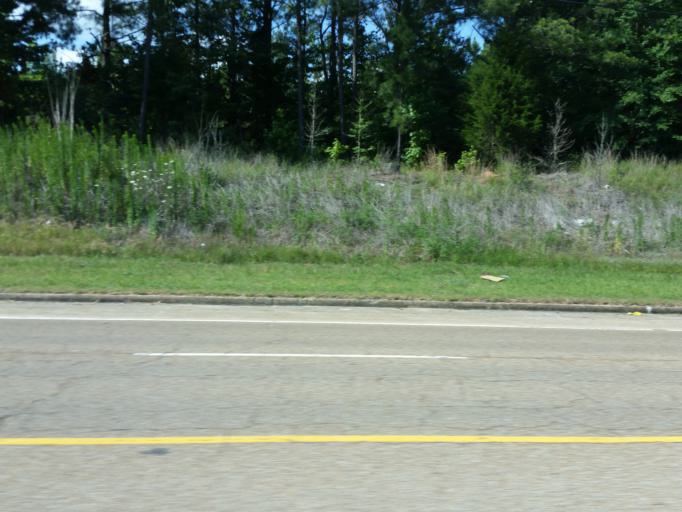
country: US
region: Tennessee
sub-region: Henderson County
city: Lexington
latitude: 35.6409
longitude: -88.3731
